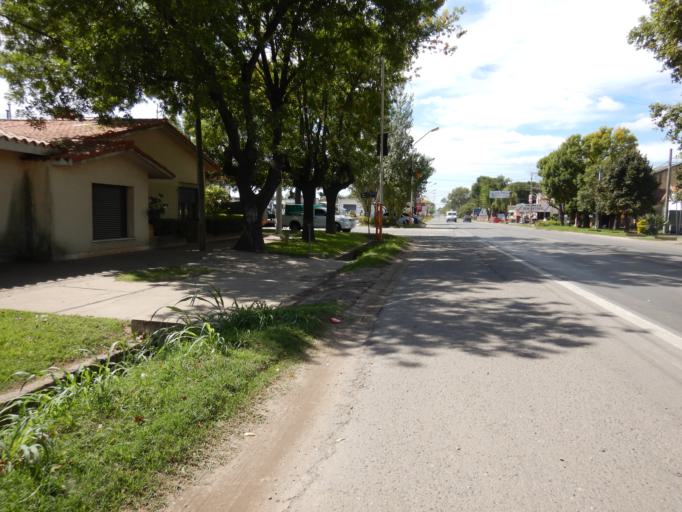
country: AR
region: Santa Fe
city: Carcarana
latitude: -32.8624
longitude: -61.1504
